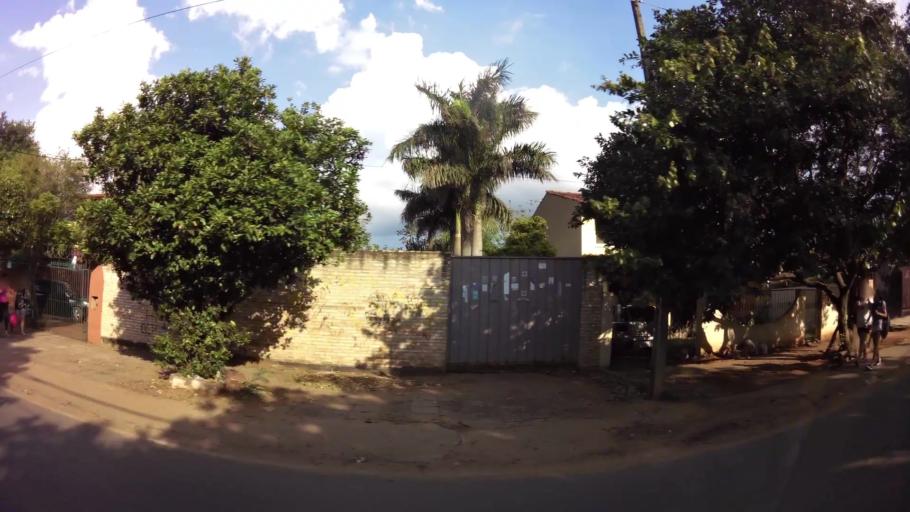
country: PY
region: Central
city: Fernando de la Mora
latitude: -25.3458
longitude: -57.5514
